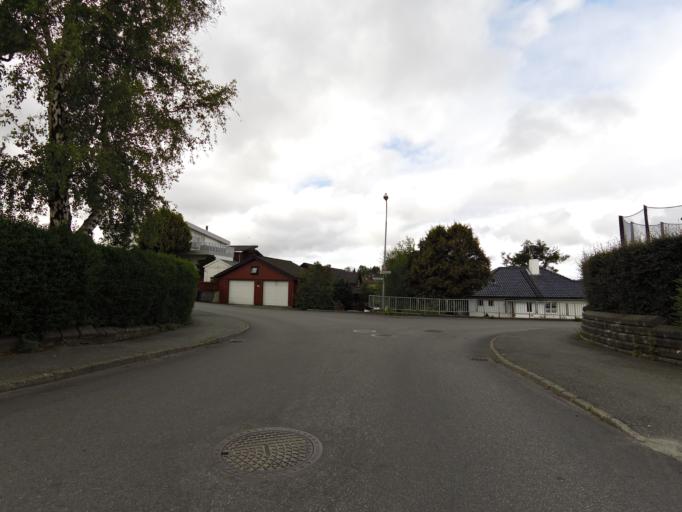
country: NO
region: Rogaland
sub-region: Stavanger
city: Stavanger
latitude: 58.9572
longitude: 5.6860
